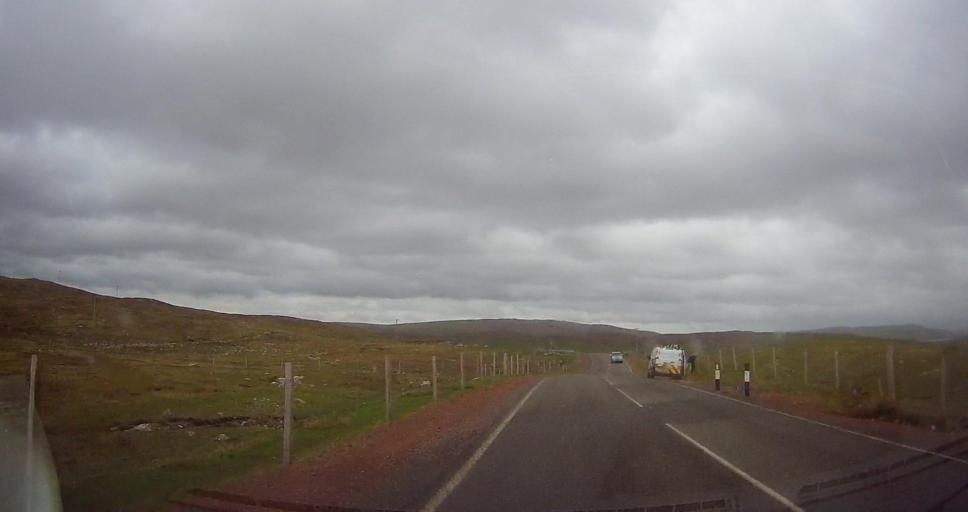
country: GB
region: Scotland
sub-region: Shetland Islands
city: Lerwick
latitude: 60.4794
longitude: -1.4410
